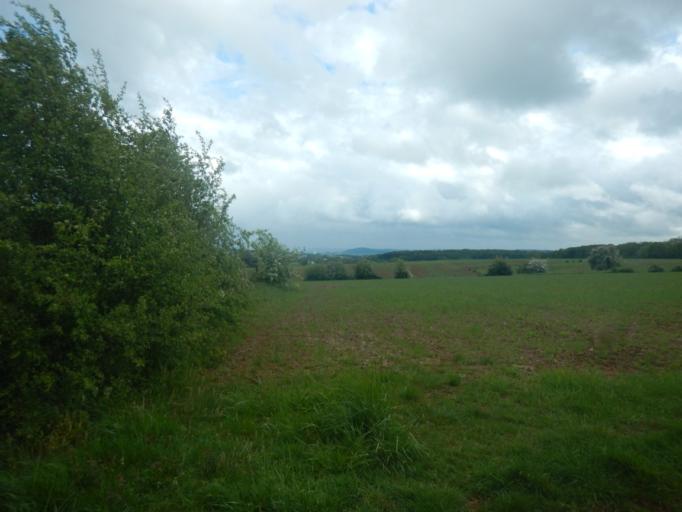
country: LU
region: Luxembourg
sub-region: Canton d'Esch-sur-Alzette
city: Reckange-sur-Mess
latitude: 49.5599
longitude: 6.0003
